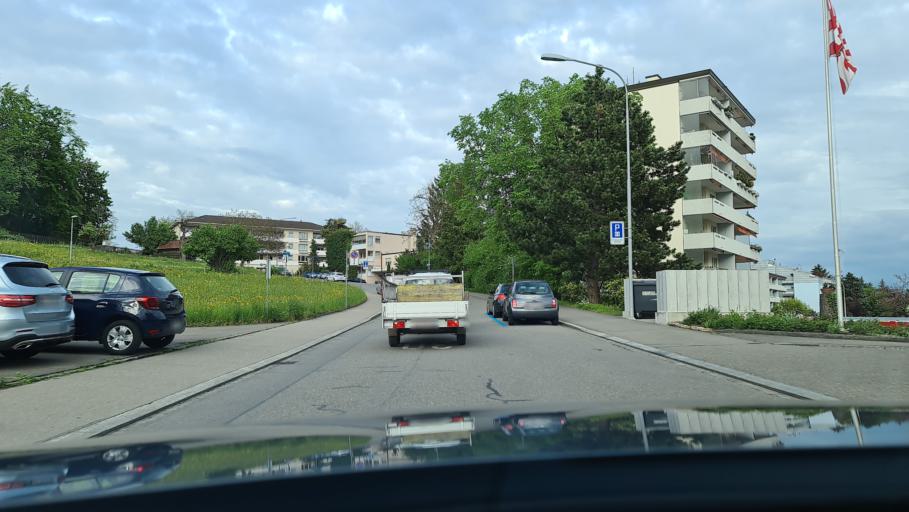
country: CH
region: Zurich
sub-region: Bezirk Zuerich
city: Zuerich (Kreis 11) / Seebach
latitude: 47.4300
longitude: 8.5388
